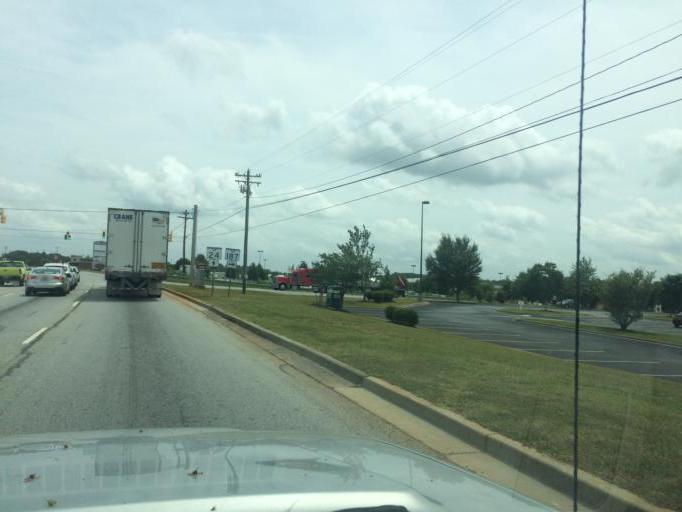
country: US
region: South Carolina
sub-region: Anderson County
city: Centerville
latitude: 34.5114
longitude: -82.7614
